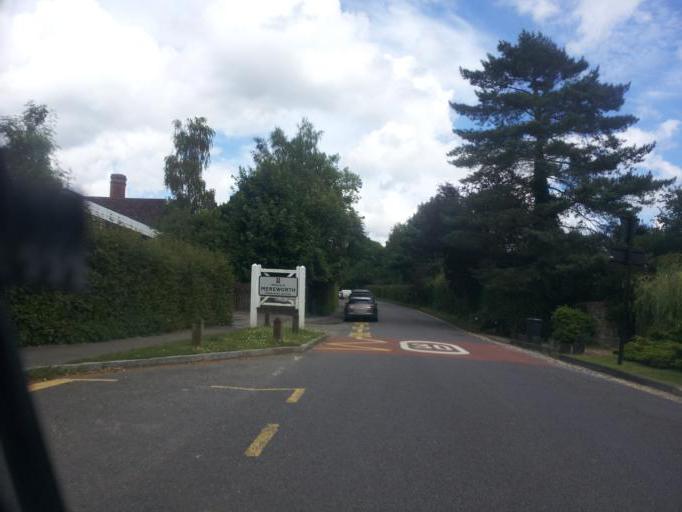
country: GB
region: England
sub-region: Kent
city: Kings Hill
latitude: 51.2564
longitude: 0.3700
